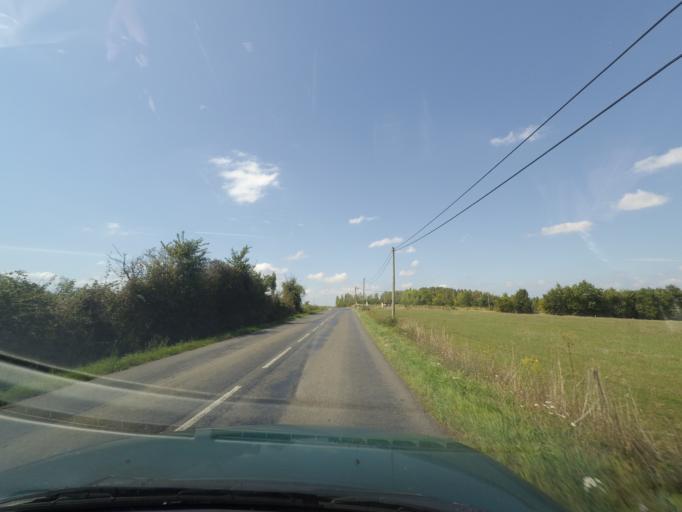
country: FR
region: Pays de la Loire
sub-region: Departement de la Loire-Atlantique
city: Saint-Lumine-de-Coutais
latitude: 47.0441
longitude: -1.7171
